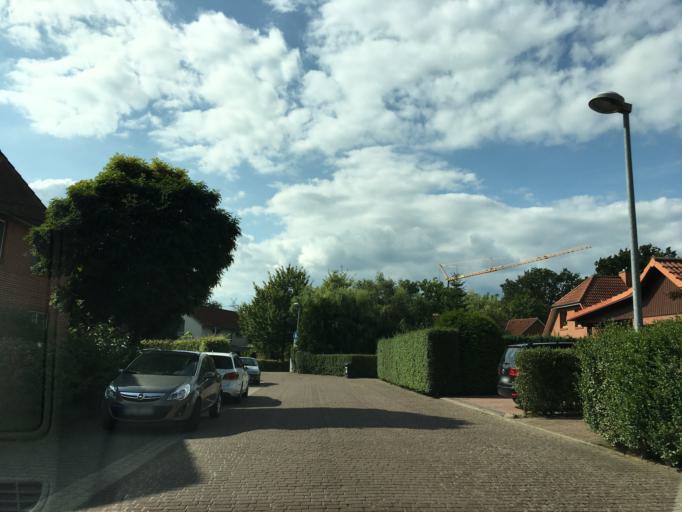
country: DE
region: Lower Saxony
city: Melbeck
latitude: 53.2102
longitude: 10.3903
